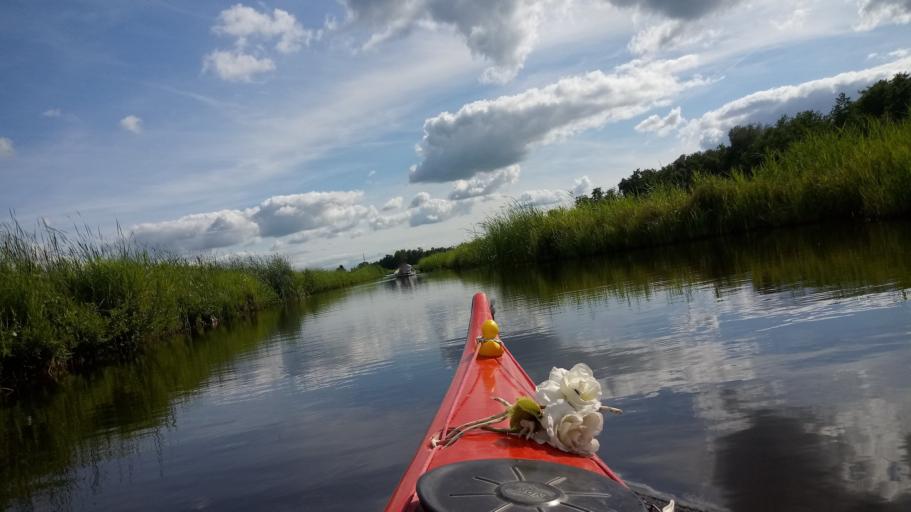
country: NL
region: Overijssel
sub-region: Gemeente Steenwijkerland
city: Wanneperveen
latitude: 52.7192
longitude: 6.1259
